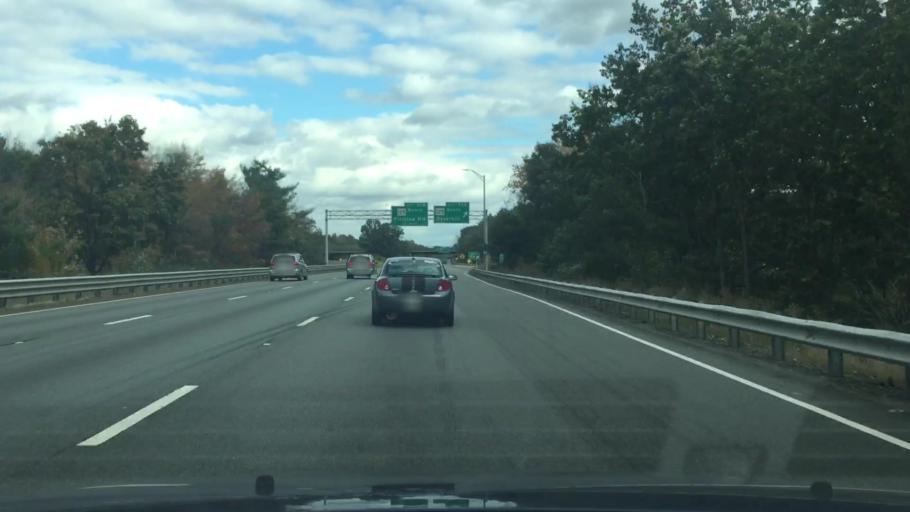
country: US
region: Massachusetts
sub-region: Essex County
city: Haverhill
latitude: 42.7959
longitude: -71.1016
